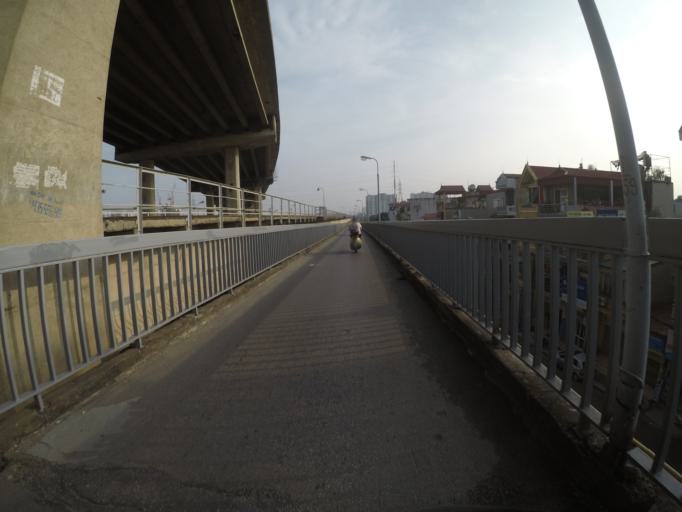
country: VN
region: Ha Noi
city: Tay Ho
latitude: 21.0899
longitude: 105.7857
